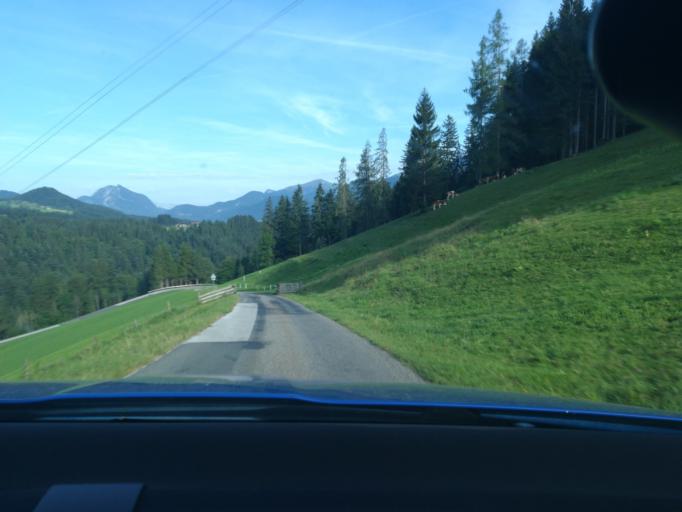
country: AT
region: Salzburg
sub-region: Politischer Bezirk Hallein
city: Abtenau
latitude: 47.5634
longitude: 13.4024
